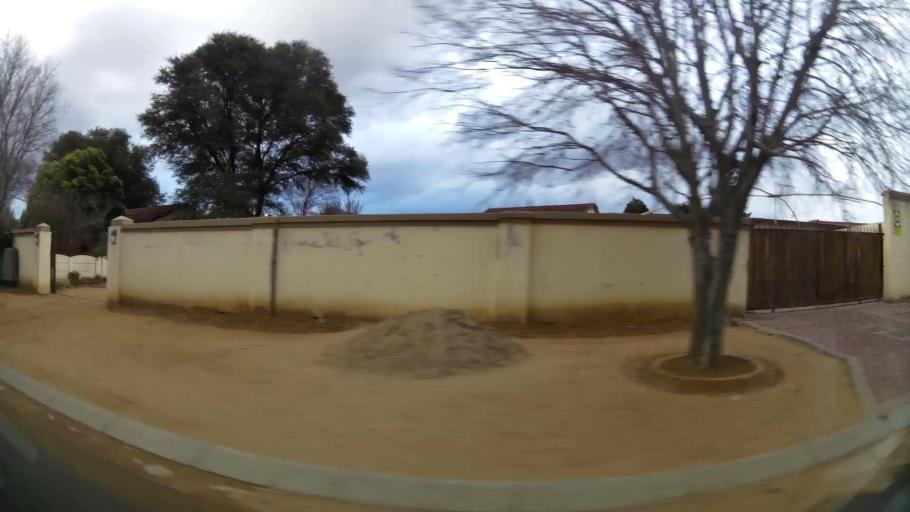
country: ZA
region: Orange Free State
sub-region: Lejweleputswa District Municipality
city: Welkom
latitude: -27.9625
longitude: 26.7239
